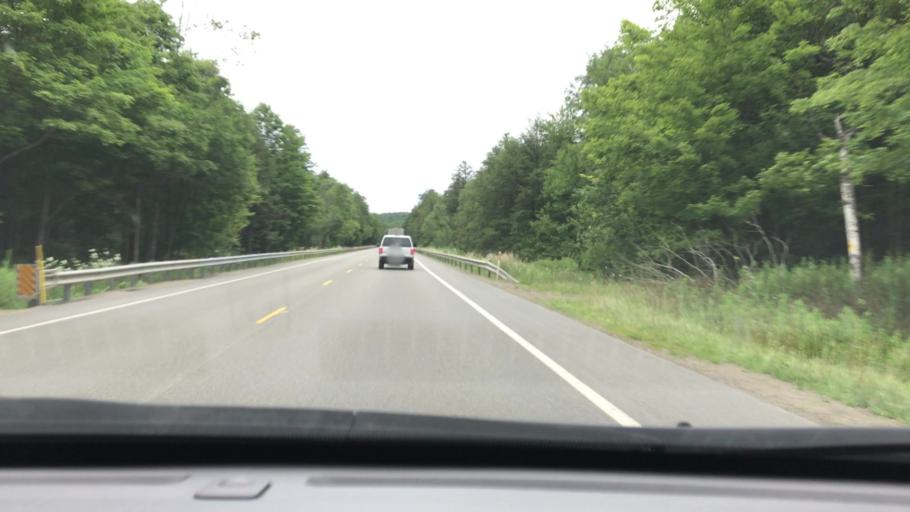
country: US
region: Pennsylvania
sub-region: McKean County
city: Kane
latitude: 41.6804
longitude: -78.6869
